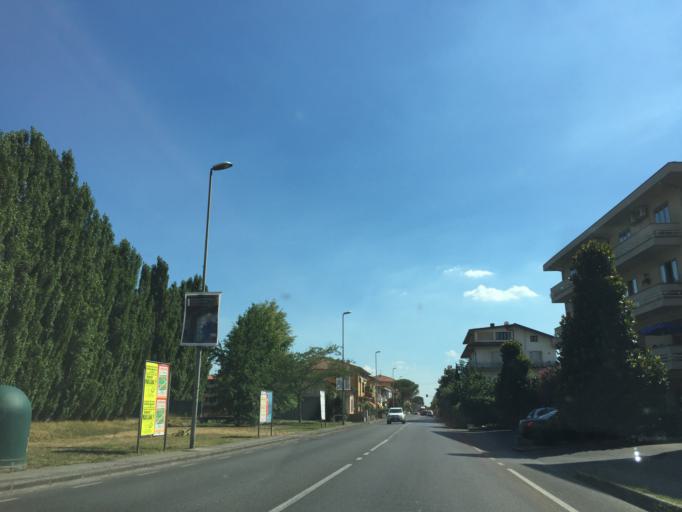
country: IT
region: Tuscany
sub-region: Provincia di Pistoia
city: Monsummano Terme
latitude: 43.8739
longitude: 10.8113
